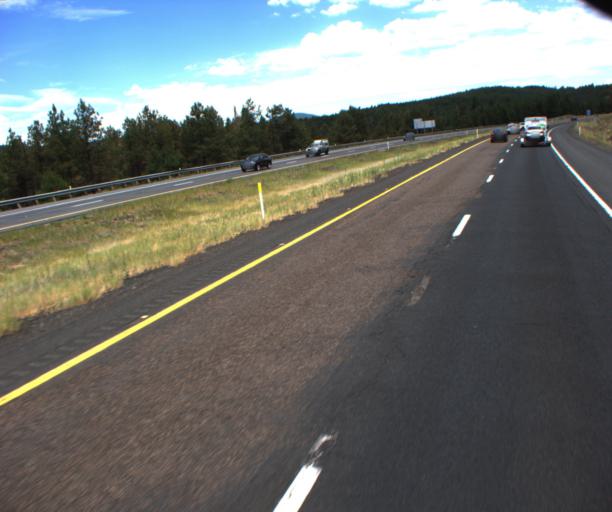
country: US
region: Arizona
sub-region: Coconino County
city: Mountainaire
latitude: 35.0604
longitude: -111.6850
